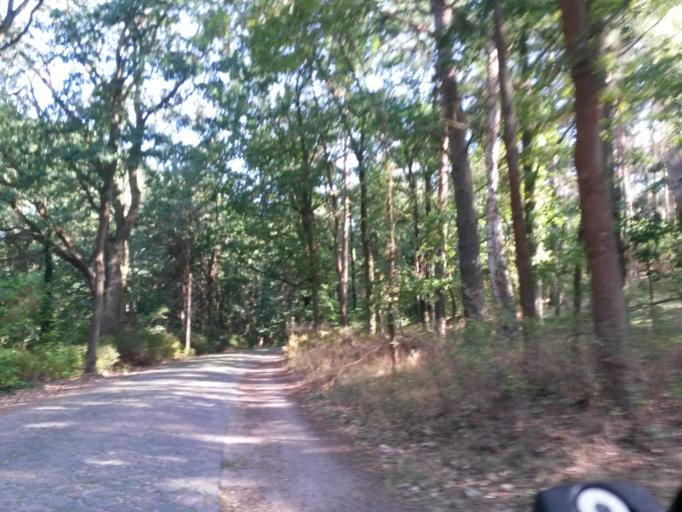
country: DE
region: Saxony-Anhalt
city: Nudersdorf
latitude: 51.9239
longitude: 12.5890
